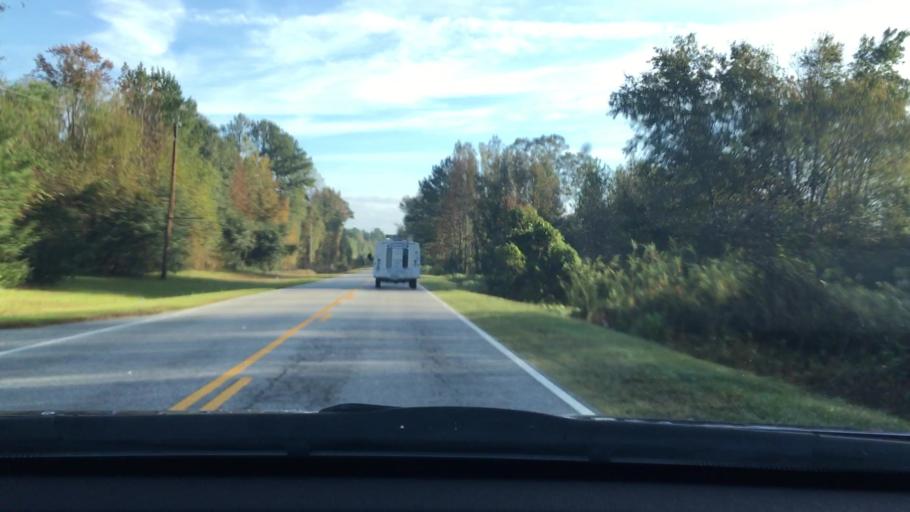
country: US
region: South Carolina
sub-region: Sumter County
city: East Sumter
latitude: 34.0416
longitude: -80.2609
